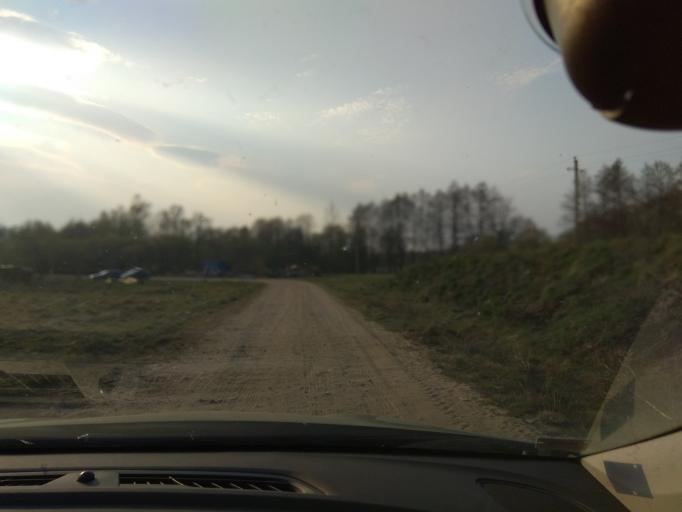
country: LT
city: Baltoji Voke
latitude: 54.5950
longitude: 25.1877
